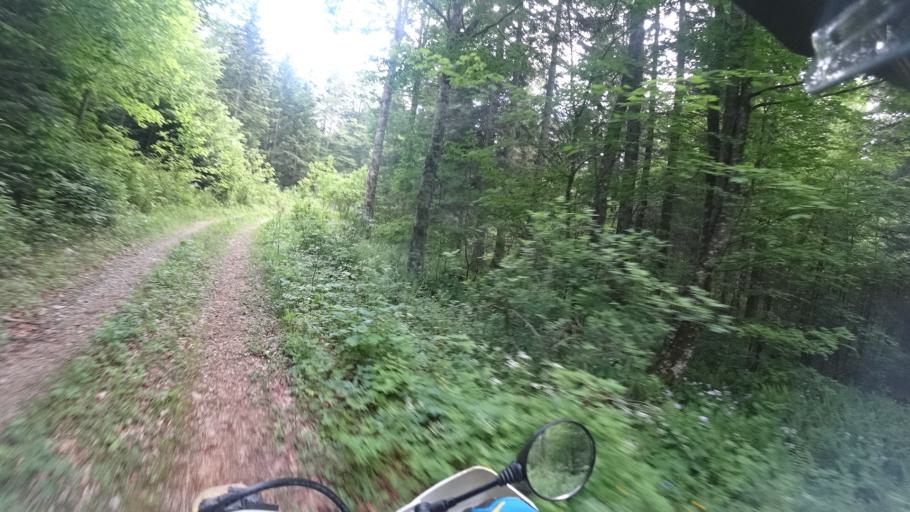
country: HR
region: Zadarska
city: Gracac
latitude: 44.4782
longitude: 15.8934
